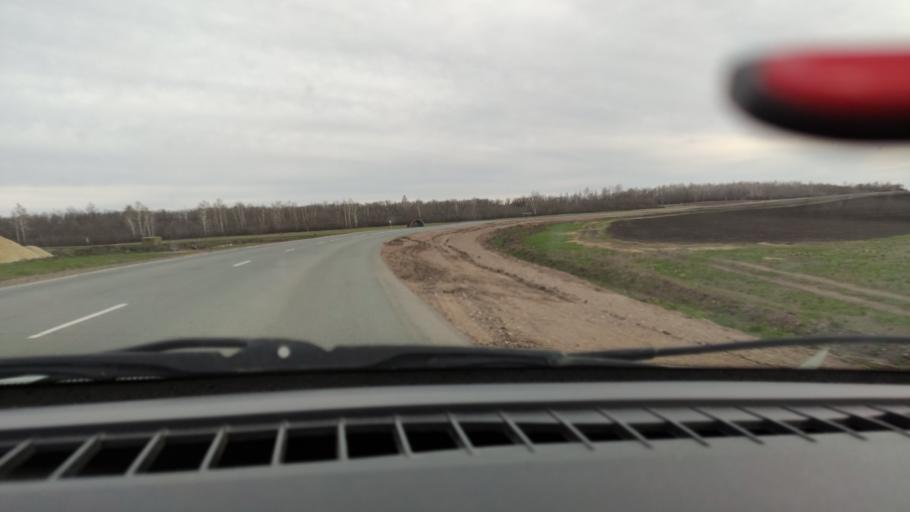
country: RU
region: Bashkortostan
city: Yermolayevo
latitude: 52.4658
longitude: 55.8309
